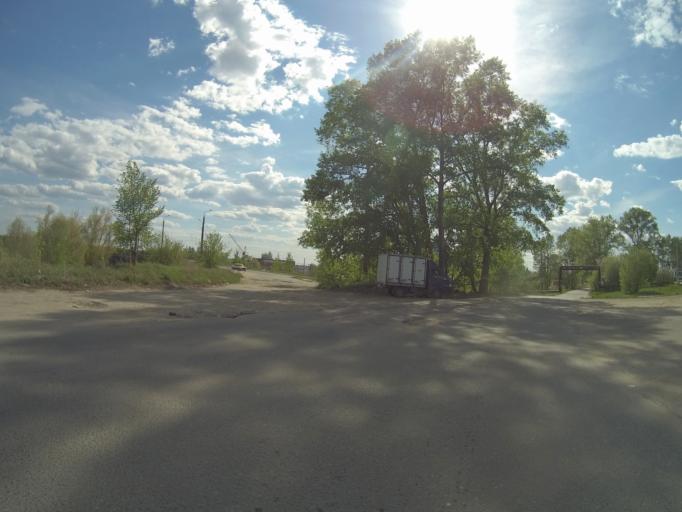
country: RU
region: Vladimir
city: Vladimir
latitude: 56.1010
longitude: 40.3489
